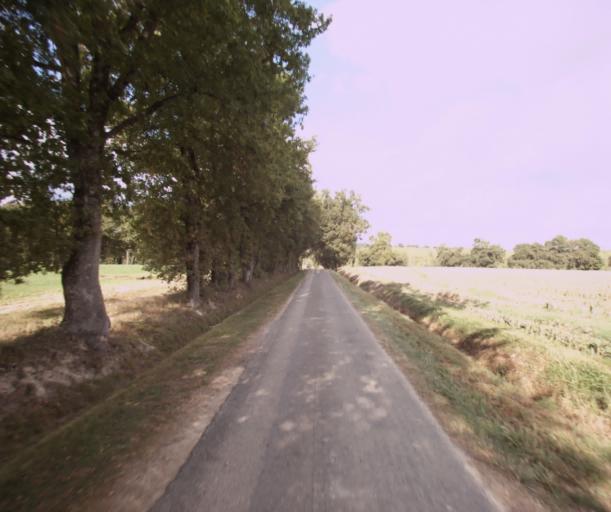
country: FR
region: Midi-Pyrenees
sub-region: Departement du Gers
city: Cazaubon
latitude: 43.9102
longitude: -0.0528
